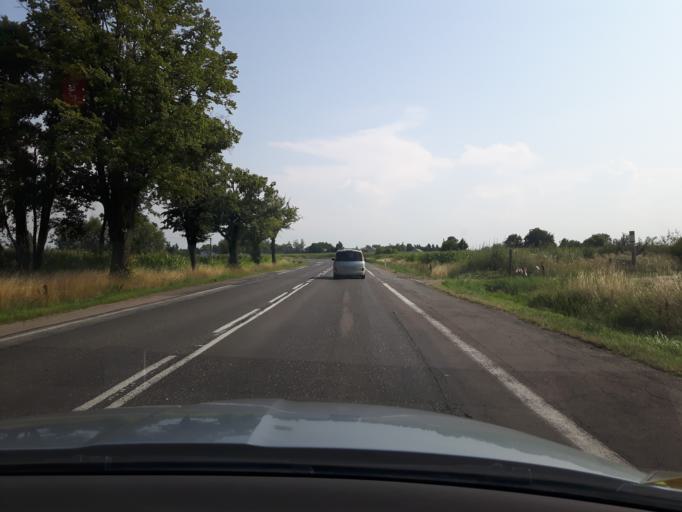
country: PL
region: Masovian Voivodeship
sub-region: Powiat plonski
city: Plonsk
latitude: 52.6632
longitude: 20.3749
